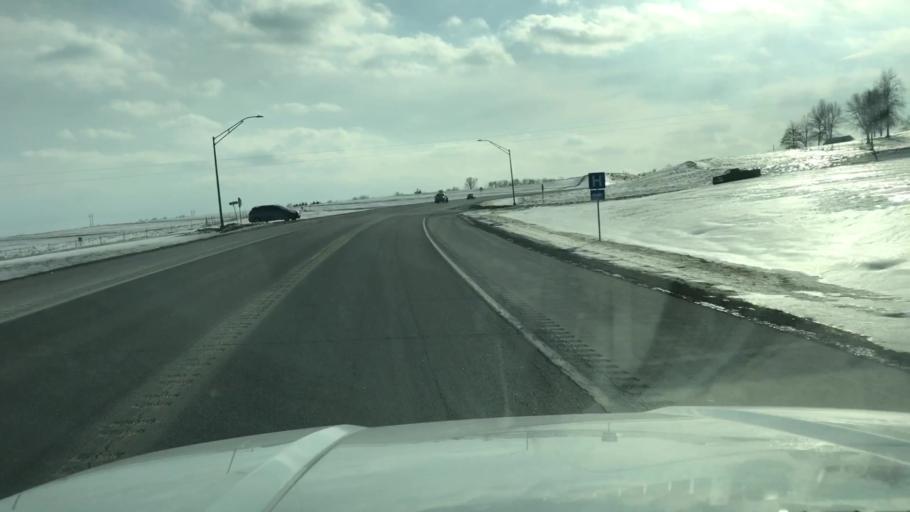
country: US
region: Missouri
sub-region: Nodaway County
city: Maryville
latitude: 40.3351
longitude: -94.8541
